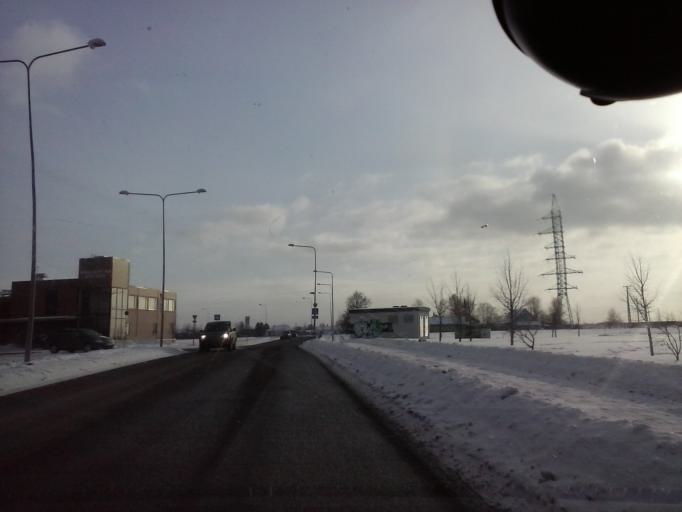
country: EE
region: Tartu
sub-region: Tartu linn
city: Tartu
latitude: 58.3587
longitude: 26.6722
